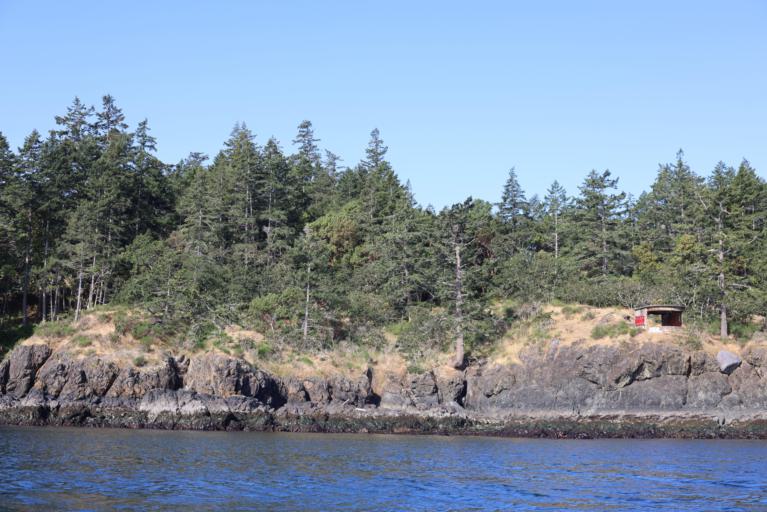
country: CA
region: British Columbia
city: Metchosin
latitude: 48.3491
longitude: -123.5401
